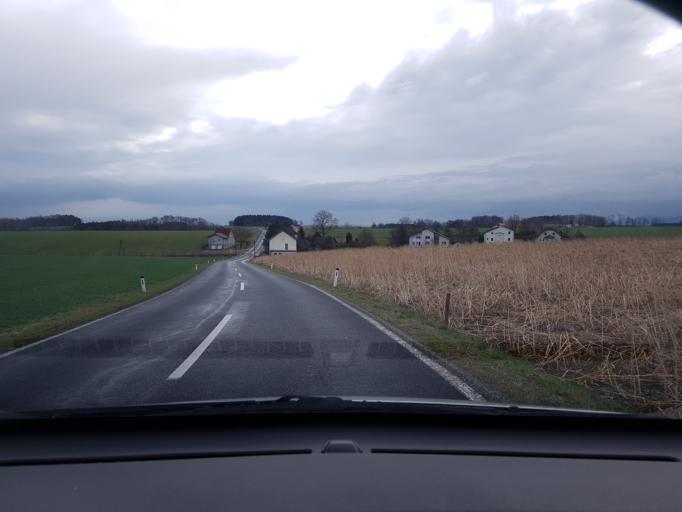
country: AT
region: Upper Austria
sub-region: Politischer Bezirk Linz-Land
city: Sankt Florian
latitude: 48.1555
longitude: 14.3480
